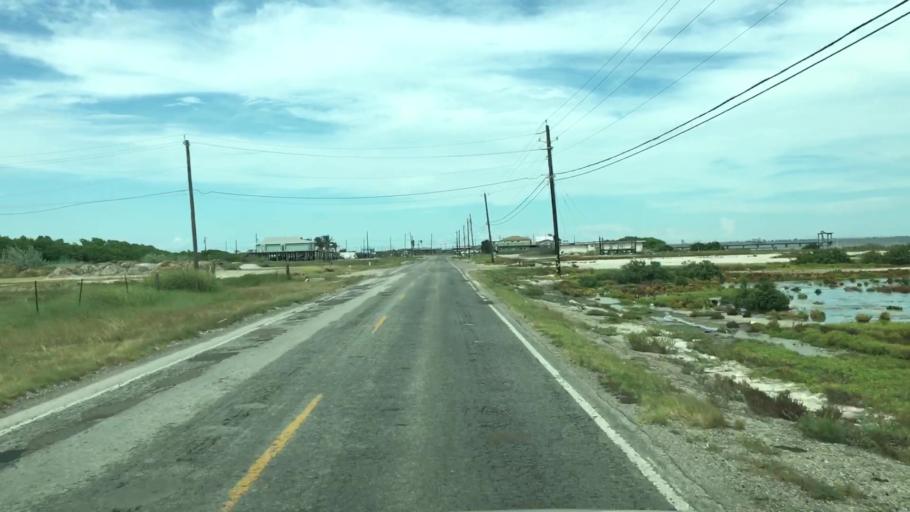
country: US
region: Texas
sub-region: Nueces County
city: Corpus Christi
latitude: 27.6332
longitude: -97.2894
